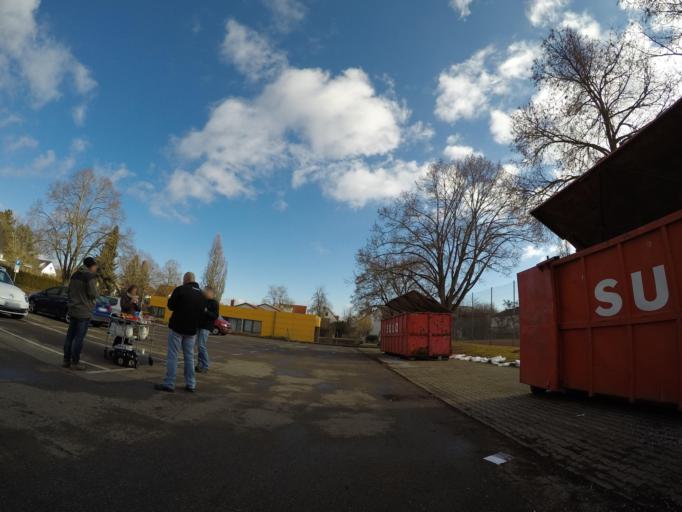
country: DE
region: Baden-Wuerttemberg
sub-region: Tuebingen Region
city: Beimerstetten
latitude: 48.4453
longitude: 9.9873
